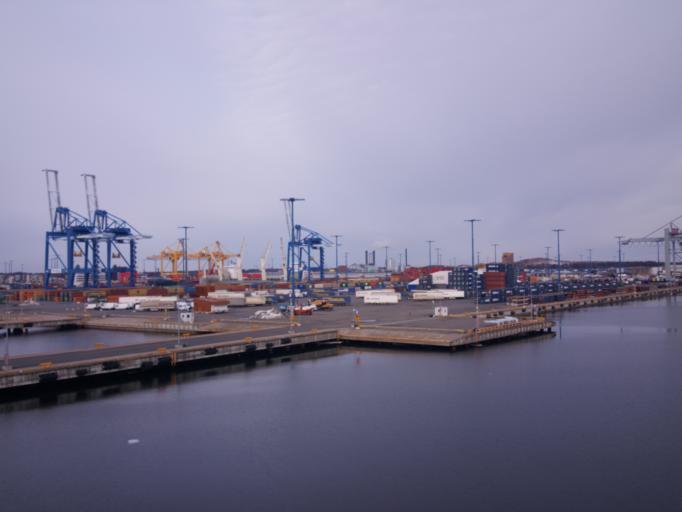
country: FI
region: Uusimaa
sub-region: Helsinki
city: Sibbo
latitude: 60.2156
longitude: 25.2045
